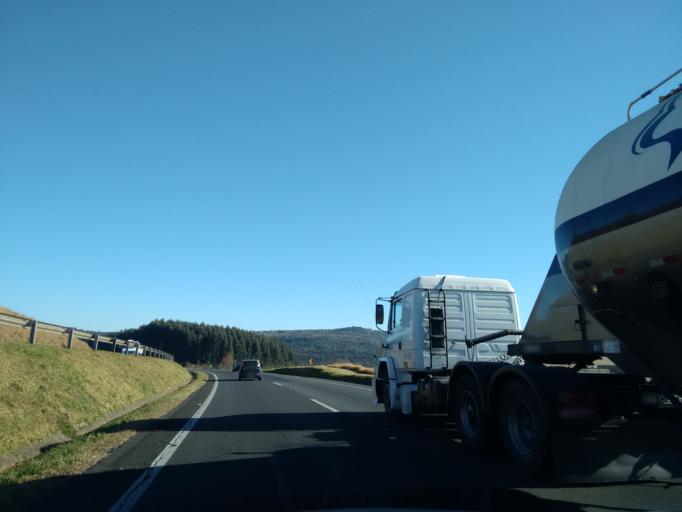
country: BR
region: Parana
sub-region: Palmeira
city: Palmeira
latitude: -25.2626
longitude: -49.9740
